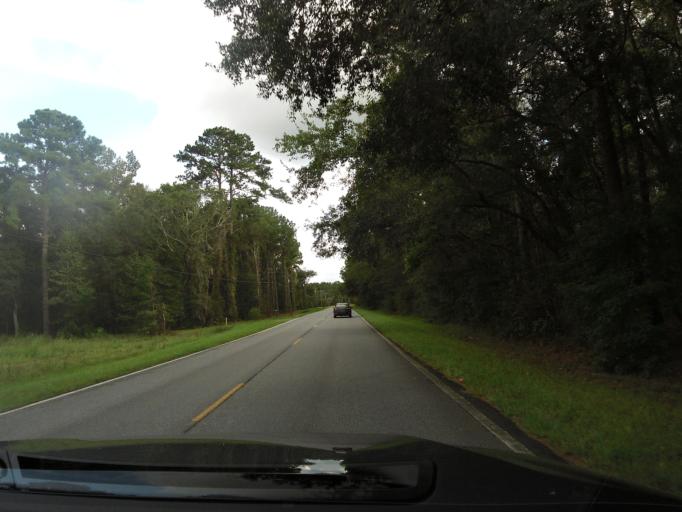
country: US
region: Georgia
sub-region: Liberty County
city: Midway
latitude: 31.8587
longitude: -81.4292
